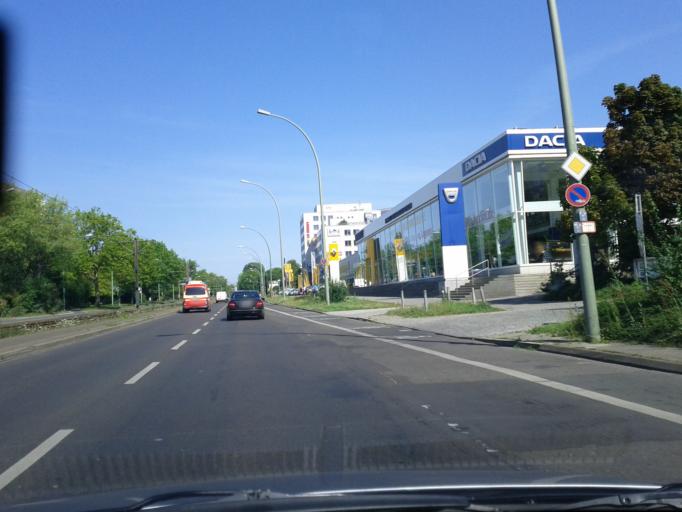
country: DE
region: Berlin
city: Fennpfuhl
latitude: 52.5337
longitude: 13.4758
